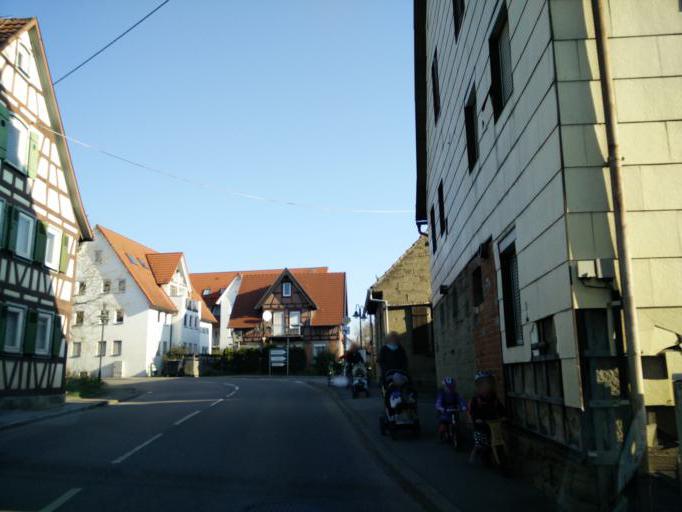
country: DE
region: Baden-Wuerttemberg
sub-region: Regierungsbezirk Stuttgart
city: Herrenberg
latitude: 48.6071
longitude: 8.8593
